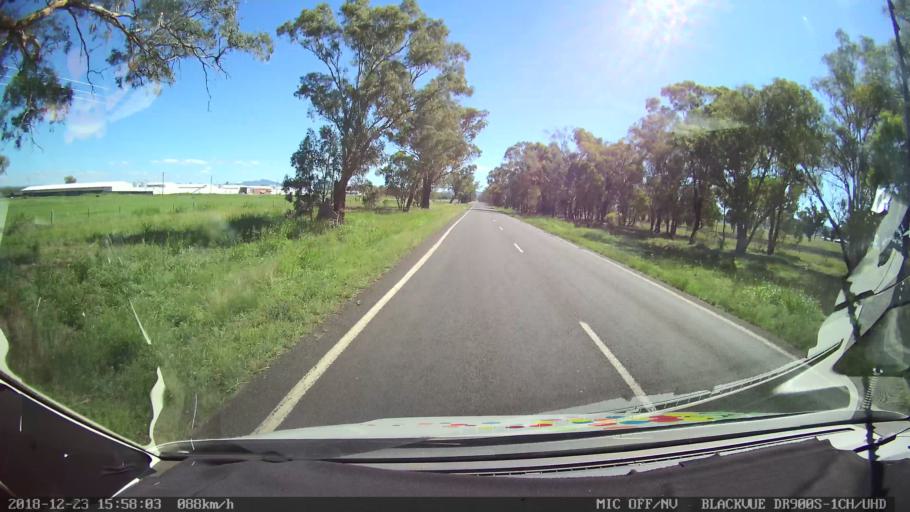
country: AU
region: New South Wales
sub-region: Tamworth Municipality
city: Phillip
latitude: -31.1839
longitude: 150.8449
